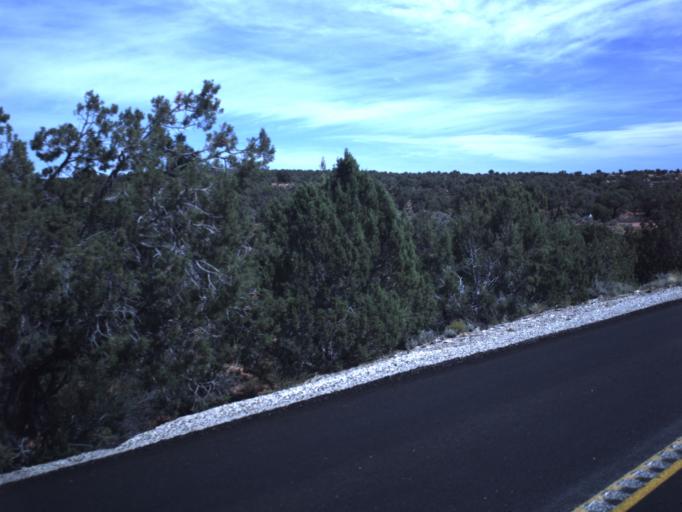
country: US
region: Utah
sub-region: San Juan County
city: Blanding
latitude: 37.5775
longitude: -109.5174
